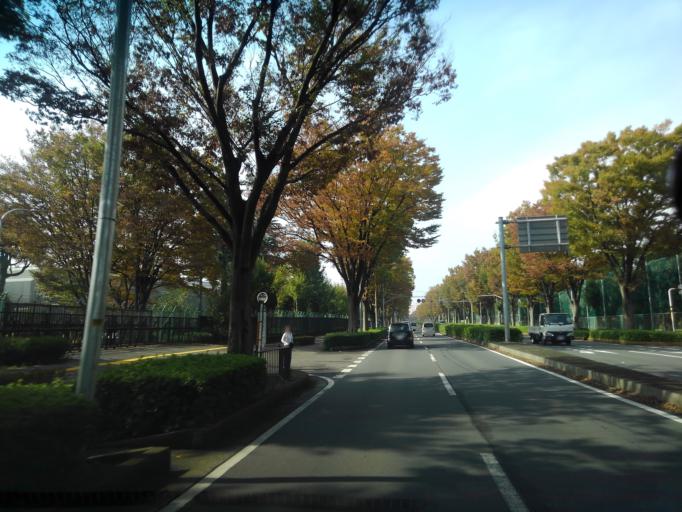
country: JP
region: Saitama
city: Tokorozawa
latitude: 35.8021
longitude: 139.4793
